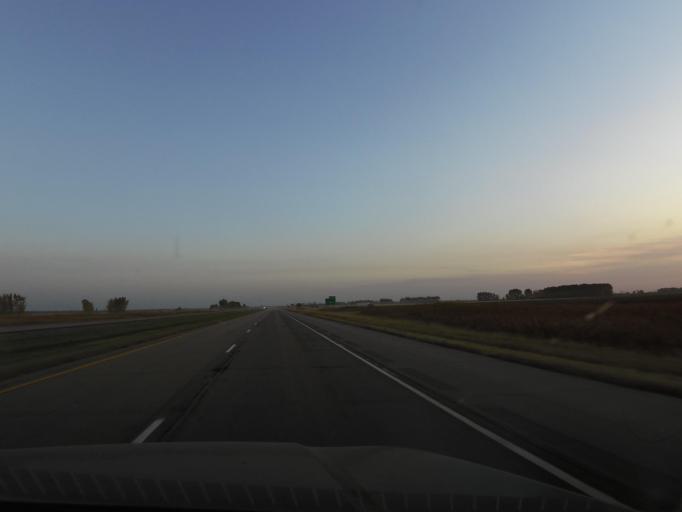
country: US
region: Minnesota
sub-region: Kittson County
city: Hallock
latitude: 48.6504
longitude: -97.1822
